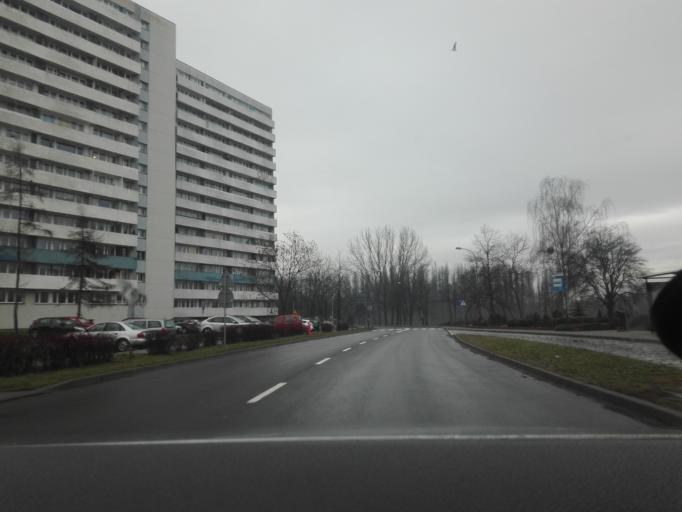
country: PL
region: Silesian Voivodeship
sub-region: Chorzow
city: Chorzow
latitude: 50.2739
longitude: 18.9810
